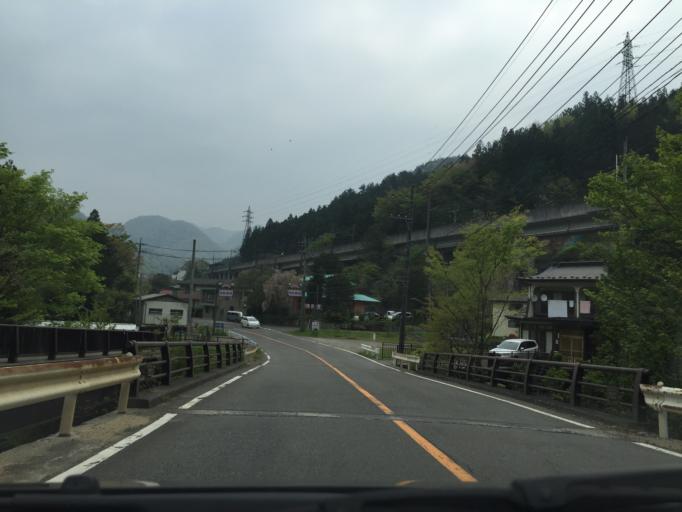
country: JP
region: Tochigi
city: Nikko
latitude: 36.8817
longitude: 139.7028
